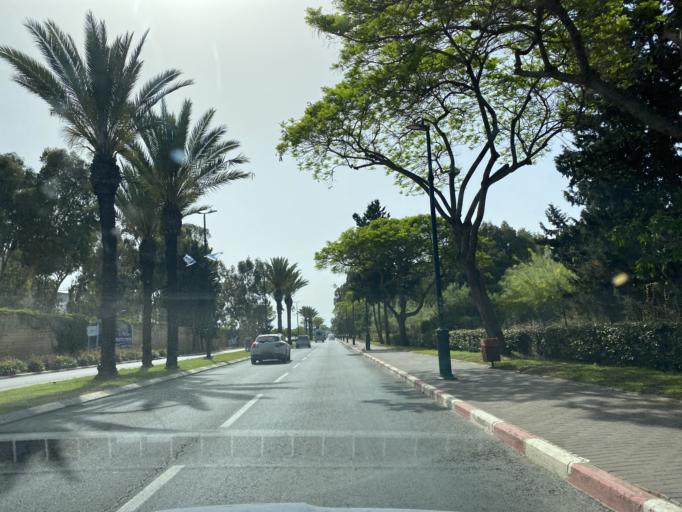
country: IL
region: Tel Aviv
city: Herzliyya
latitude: 32.1778
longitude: 34.8363
